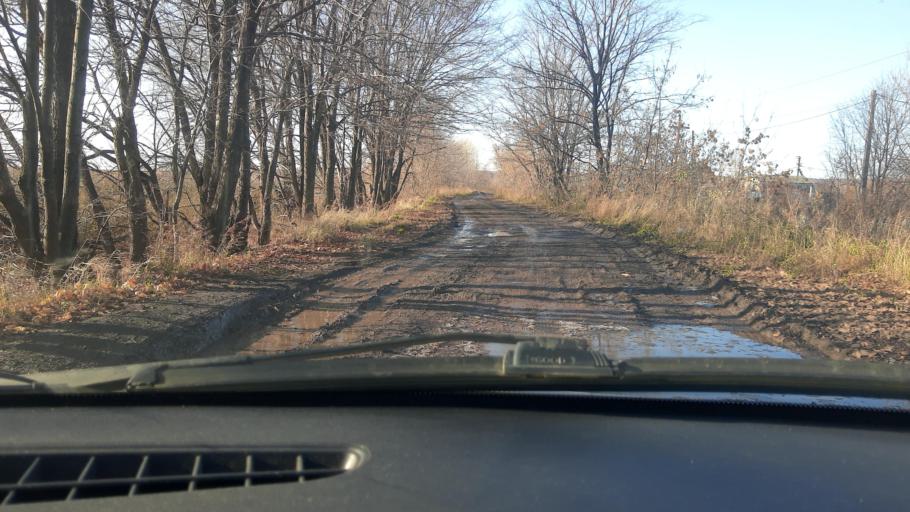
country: RU
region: Bashkortostan
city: Avdon
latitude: 54.7160
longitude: 55.7878
